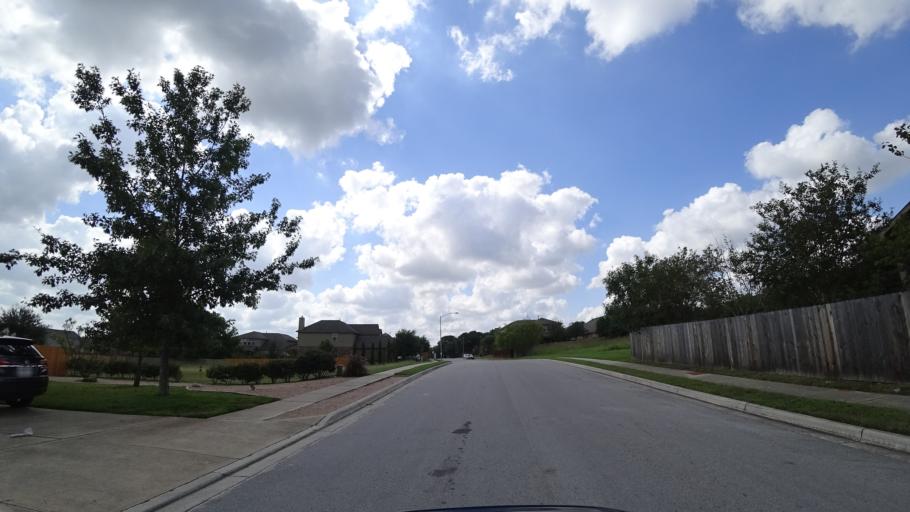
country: US
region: Texas
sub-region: Travis County
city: Onion Creek
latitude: 30.1873
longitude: -97.7987
